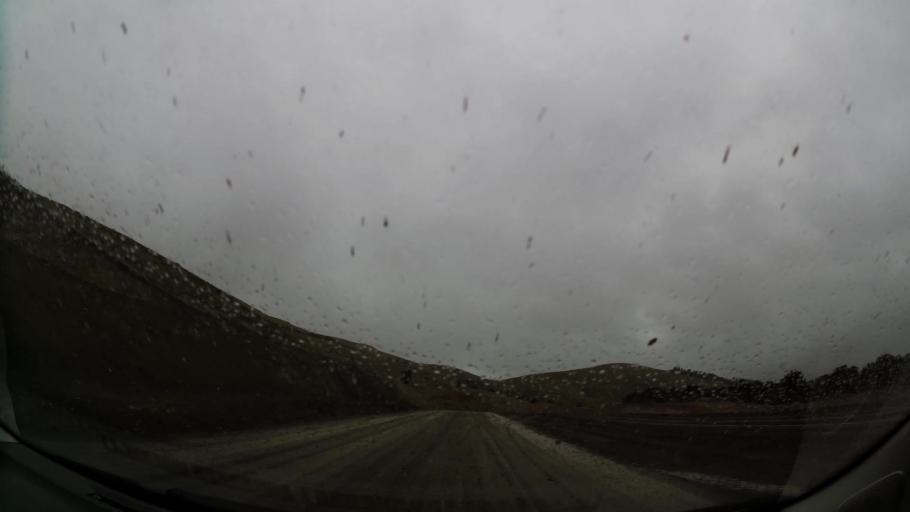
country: MA
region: Taza-Al Hoceima-Taounate
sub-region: Taza
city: Ajdir
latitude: 34.9021
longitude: -3.7889
